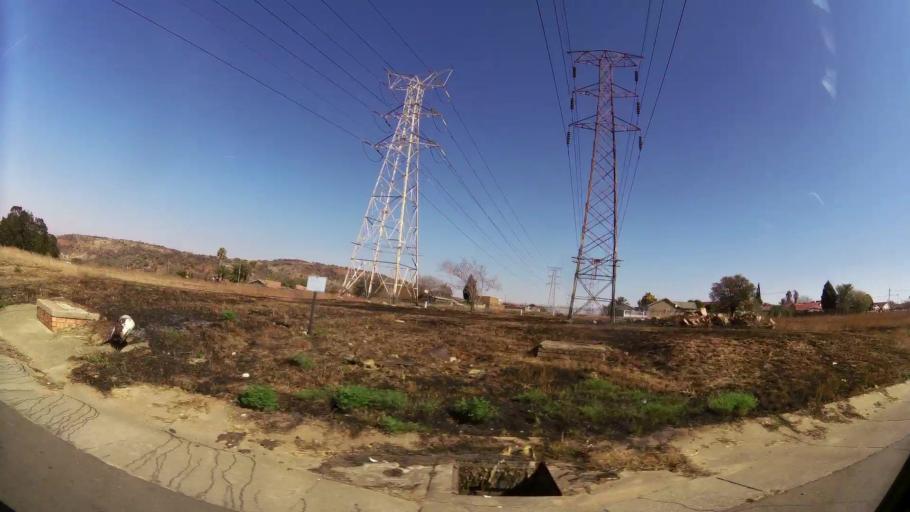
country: ZA
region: Gauteng
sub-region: City of Johannesburg Metropolitan Municipality
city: Johannesburg
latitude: -26.2750
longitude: 28.0344
